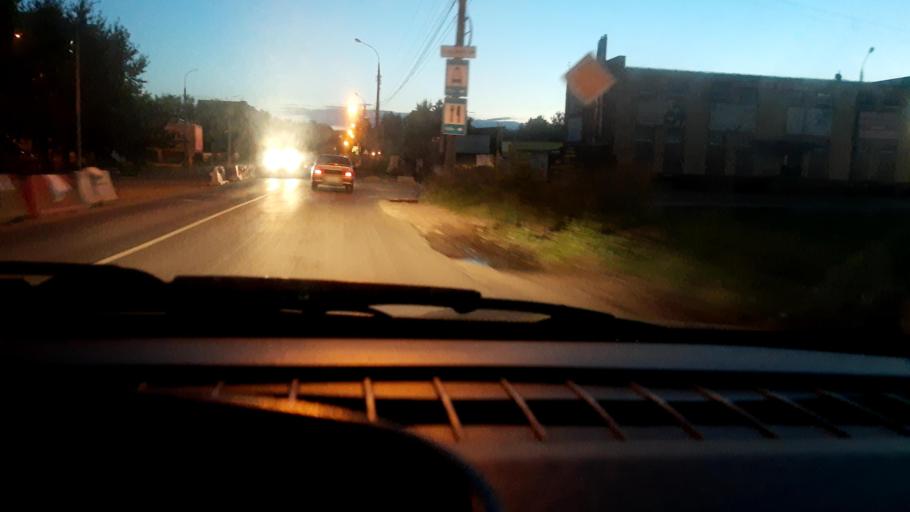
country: RU
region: Nizjnij Novgorod
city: Dzerzhinsk
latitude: 56.2470
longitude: 43.3959
